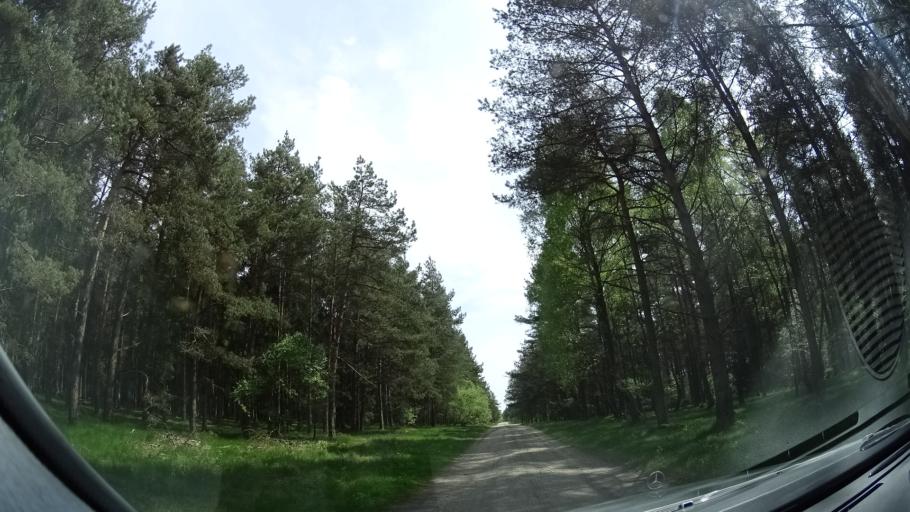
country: SE
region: Skane
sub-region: Sjobo Kommun
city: Sjoebo
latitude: 55.6687
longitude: 13.6446
